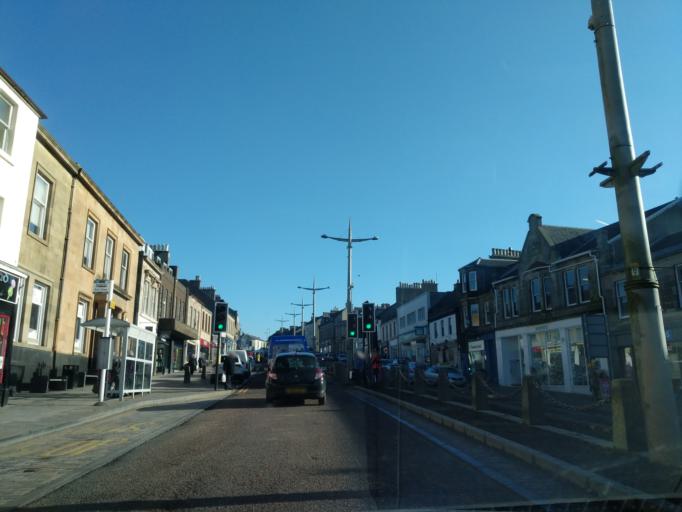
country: GB
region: Scotland
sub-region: South Lanarkshire
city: Lanark
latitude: 55.6736
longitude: -3.7789
